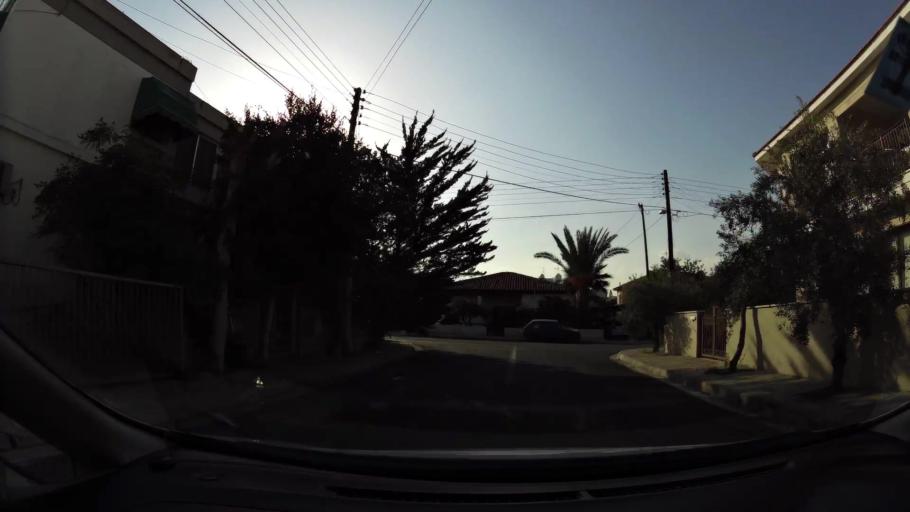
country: CY
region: Lefkosia
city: Nicosia
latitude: 35.1742
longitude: 33.3356
